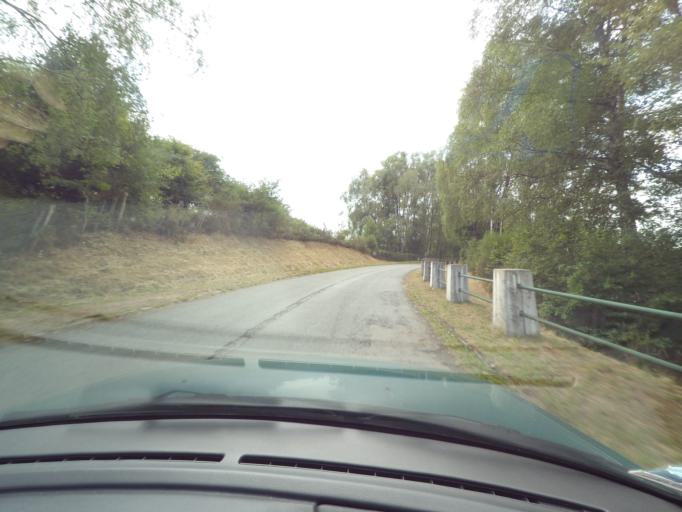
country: FR
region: Limousin
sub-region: Departement de la Correze
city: Bugeat
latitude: 45.7310
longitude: 1.9975
